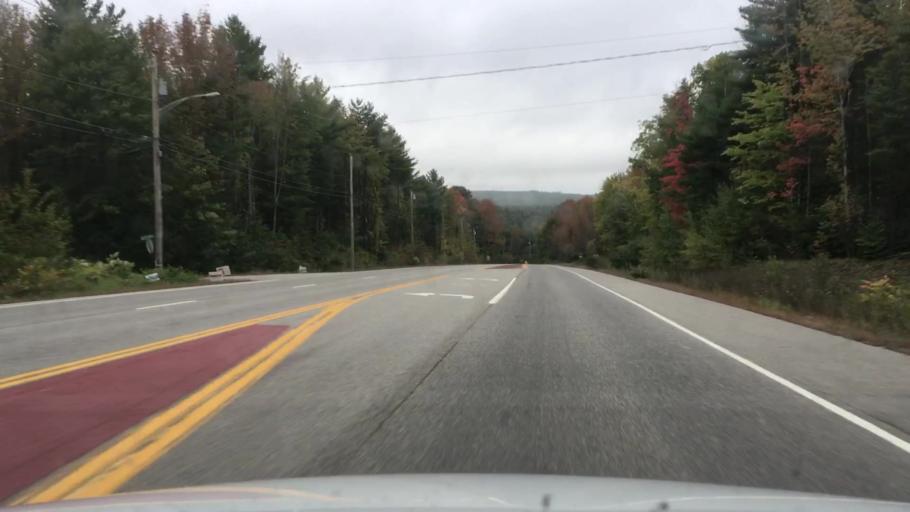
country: US
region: Maine
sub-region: Androscoggin County
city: Poland
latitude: 44.0323
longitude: -70.3684
